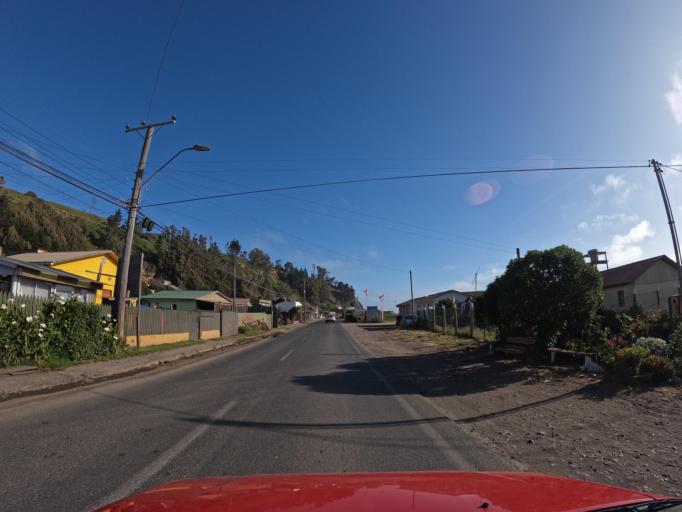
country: CL
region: Maule
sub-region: Provincia de Talca
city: Constitucion
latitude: -34.9037
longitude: -72.1799
